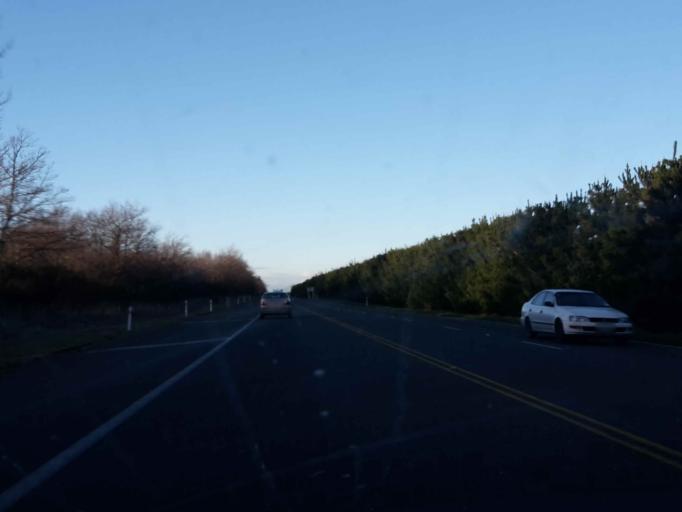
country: NZ
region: Canterbury
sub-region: Selwyn District
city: Burnham
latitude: -43.6304
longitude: 172.2747
